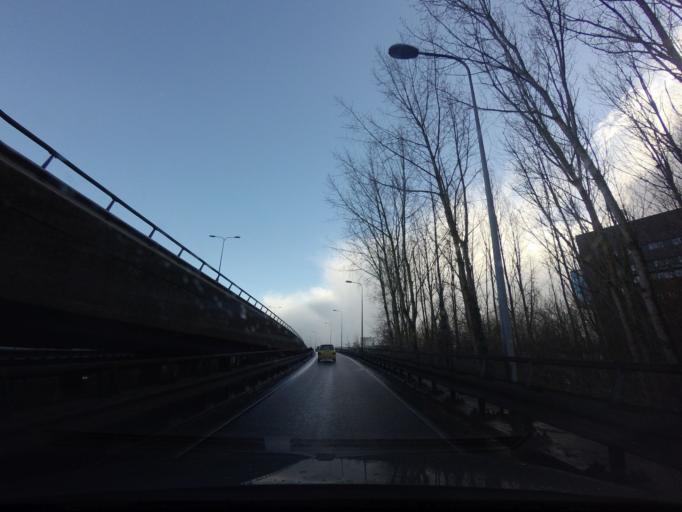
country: NL
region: Groningen
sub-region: Gemeente Groningen
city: Groningen
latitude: 53.2106
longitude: 6.5453
